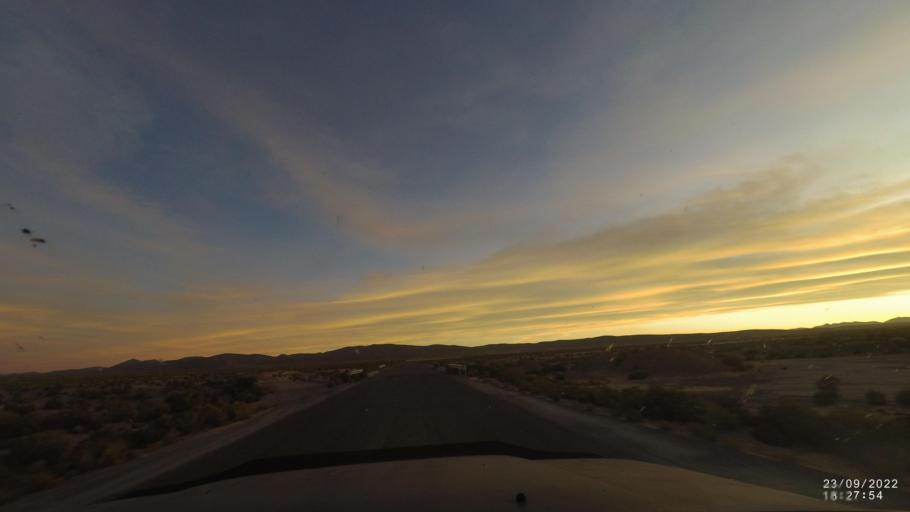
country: BO
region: Oruro
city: Challapata
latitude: -19.3321
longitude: -67.1727
